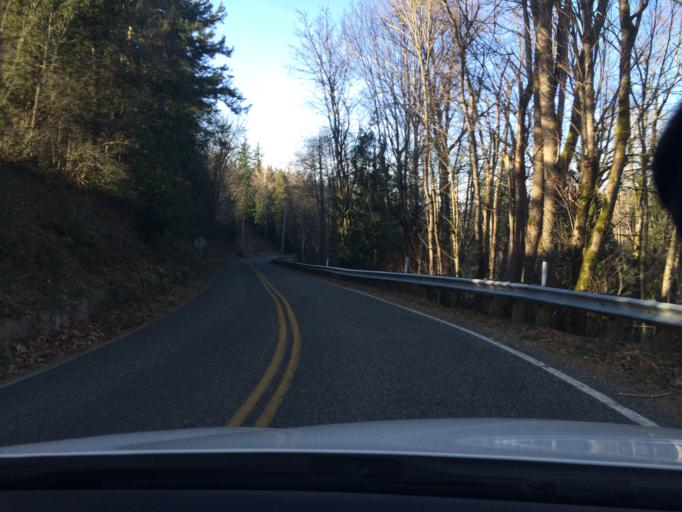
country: US
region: Washington
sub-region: Whatcom County
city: Everson
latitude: 48.8459
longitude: -122.3971
